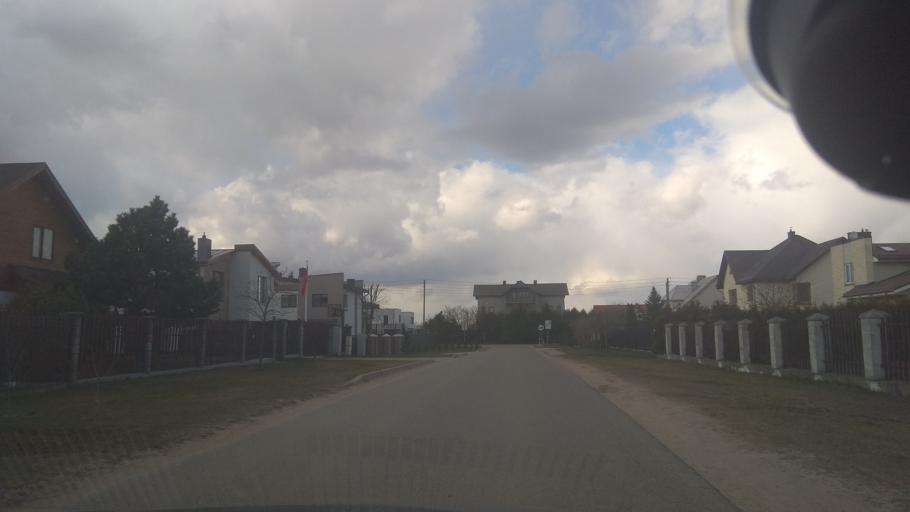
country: LT
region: Vilnius County
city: Pasilaiciai
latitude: 54.7425
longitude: 25.2008
